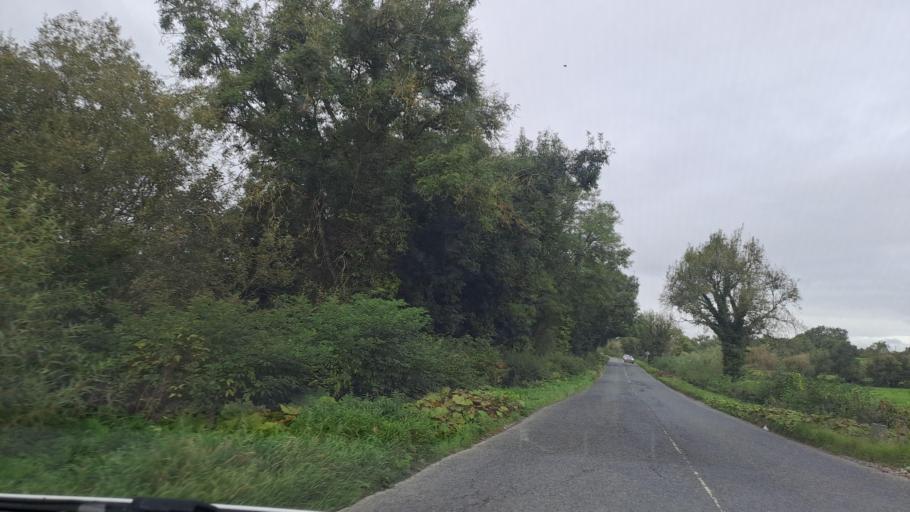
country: IE
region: Ulster
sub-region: An Cabhan
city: Kingscourt
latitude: 53.8832
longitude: -6.7361
